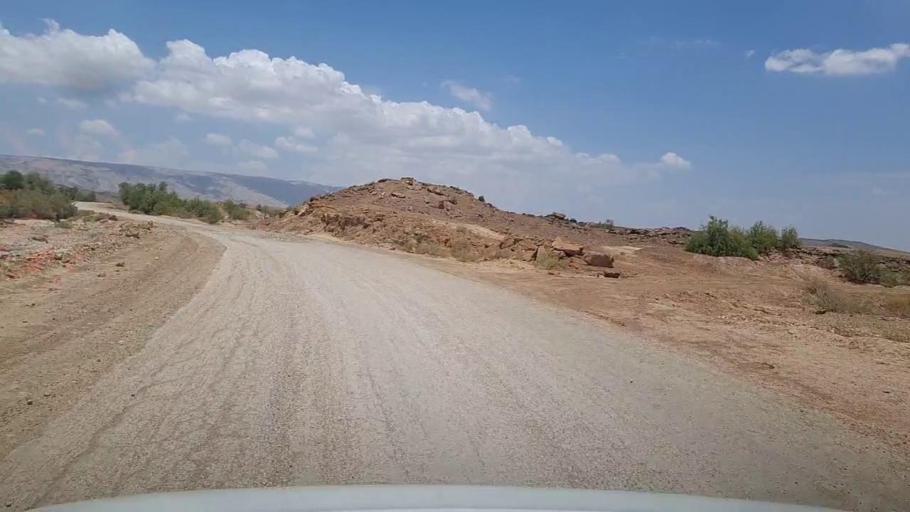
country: PK
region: Sindh
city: Bhan
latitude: 26.3173
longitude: 67.5768
